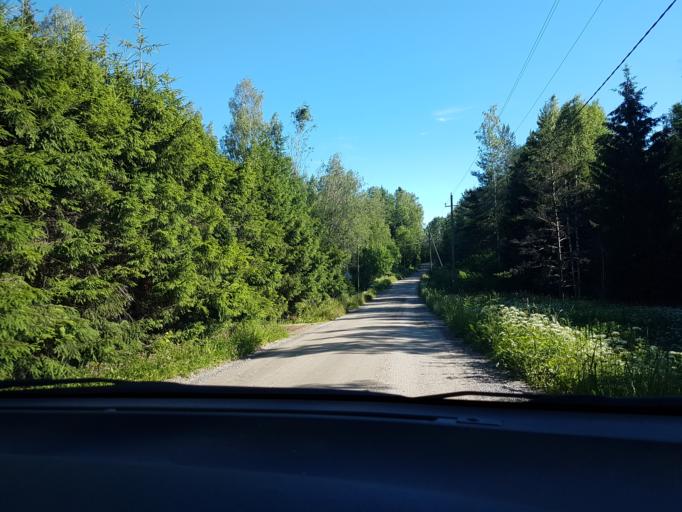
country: FI
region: Uusimaa
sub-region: Helsinki
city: Sibbo
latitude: 60.2800
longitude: 25.2371
